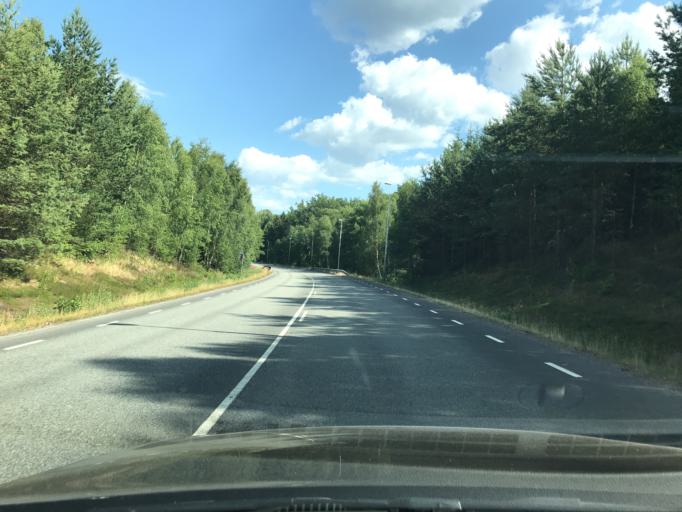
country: SE
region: Skane
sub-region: Hassleholms Kommun
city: Hastveda
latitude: 56.2785
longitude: 13.9342
